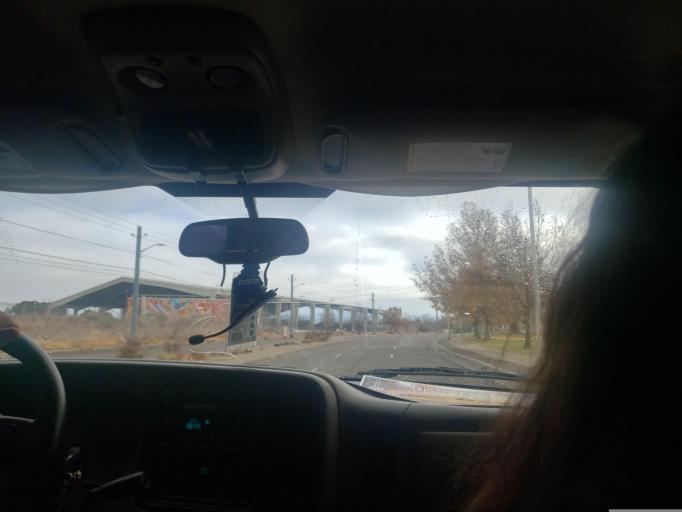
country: US
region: New Mexico
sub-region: Bernalillo County
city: Albuquerque
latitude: 35.0691
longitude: -106.6270
